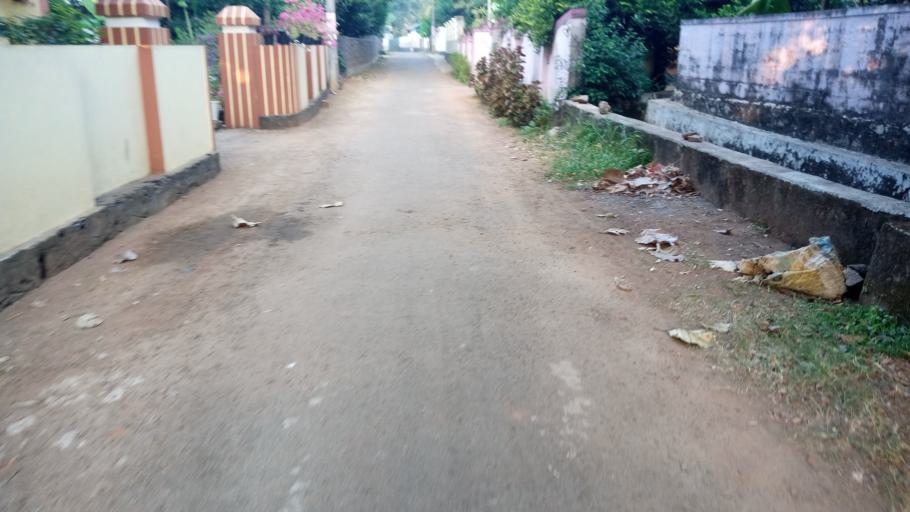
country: IN
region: Kerala
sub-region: Thrissur District
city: Kizhake Chalakudi
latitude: 10.2519
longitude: 76.3180
